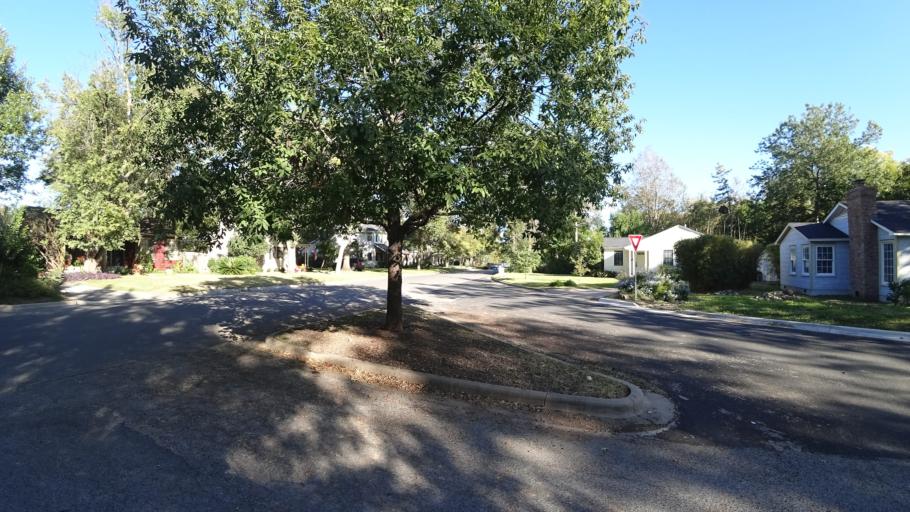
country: US
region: Texas
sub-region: Travis County
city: Austin
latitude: 30.3071
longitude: -97.7540
